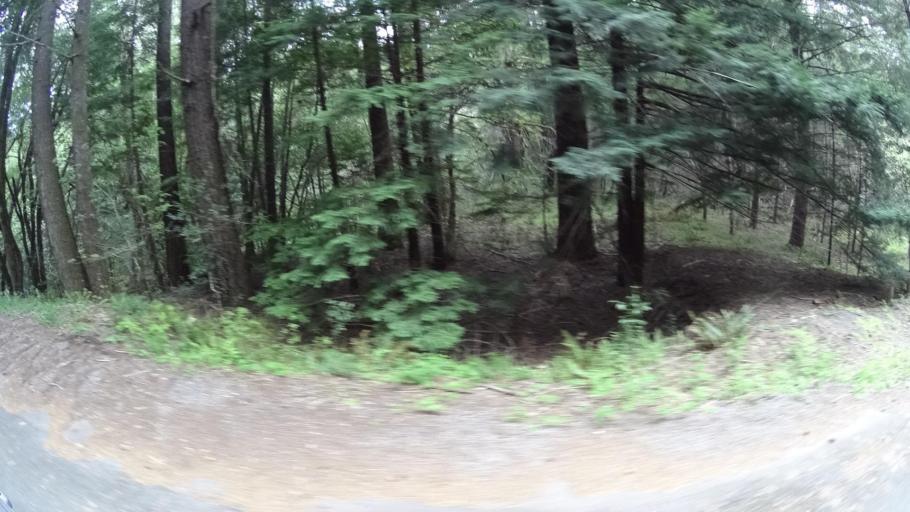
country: US
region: California
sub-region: Humboldt County
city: Redway
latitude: 40.0074
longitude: -123.9287
